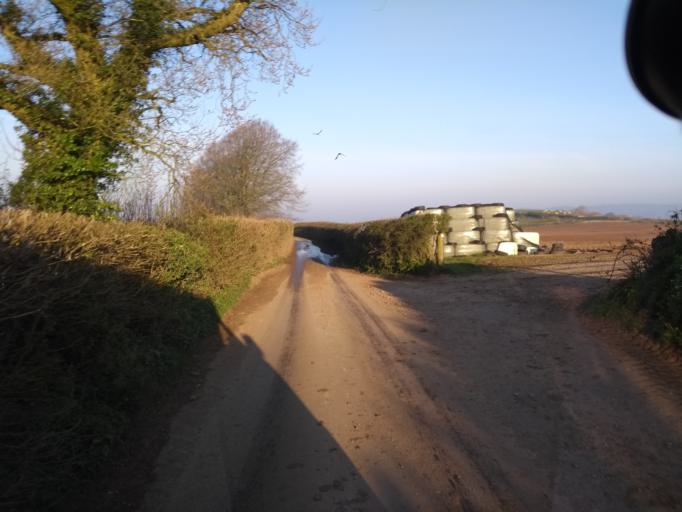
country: GB
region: England
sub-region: Somerset
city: Crewkerne
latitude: 50.8370
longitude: -2.8053
